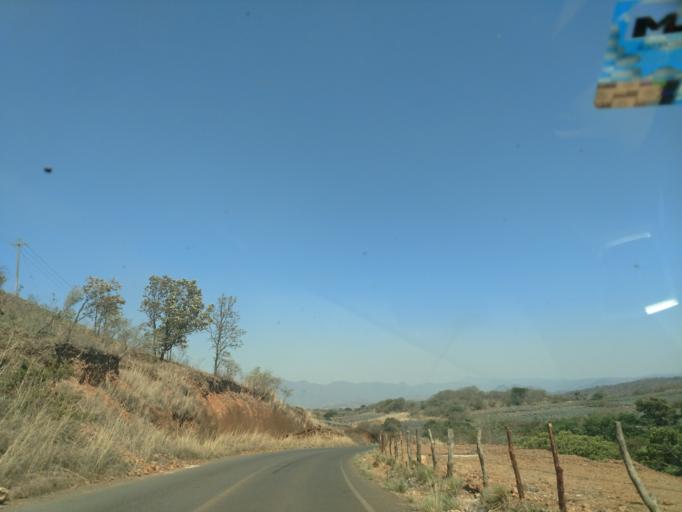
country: MX
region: Nayarit
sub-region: Tepic
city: La Corregidora
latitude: 21.4912
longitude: -104.6838
